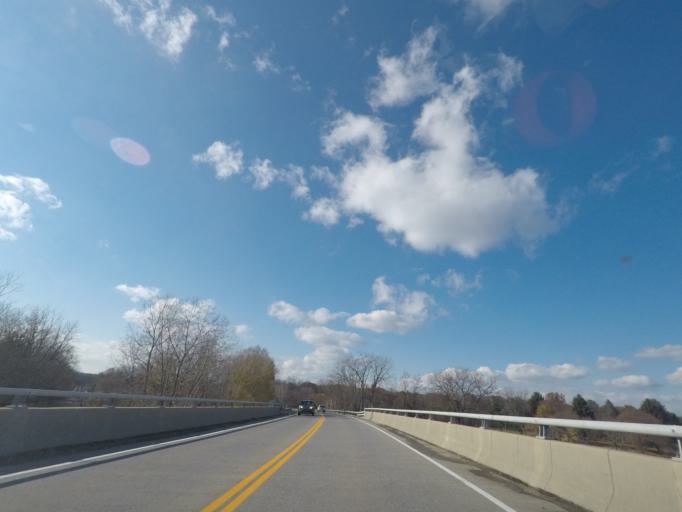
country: US
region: New York
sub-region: Saratoga County
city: Country Knolls
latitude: 42.8928
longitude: -73.8246
